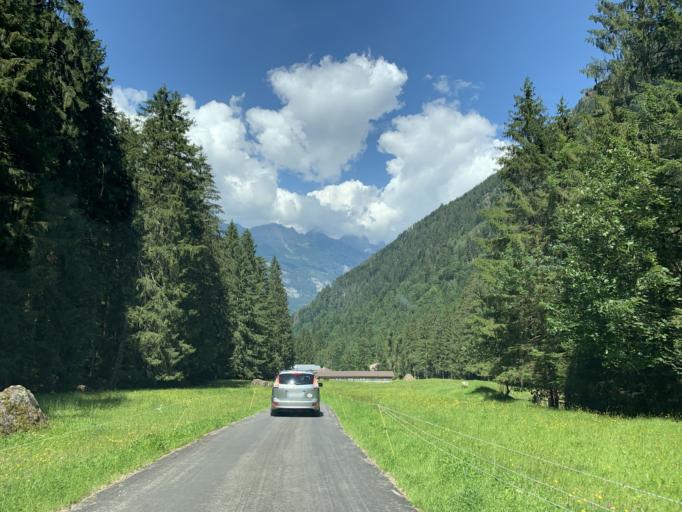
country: CH
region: Saint Gallen
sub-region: Wahlkreis Sarganserland
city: Quarten
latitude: 47.0901
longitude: 9.2057
